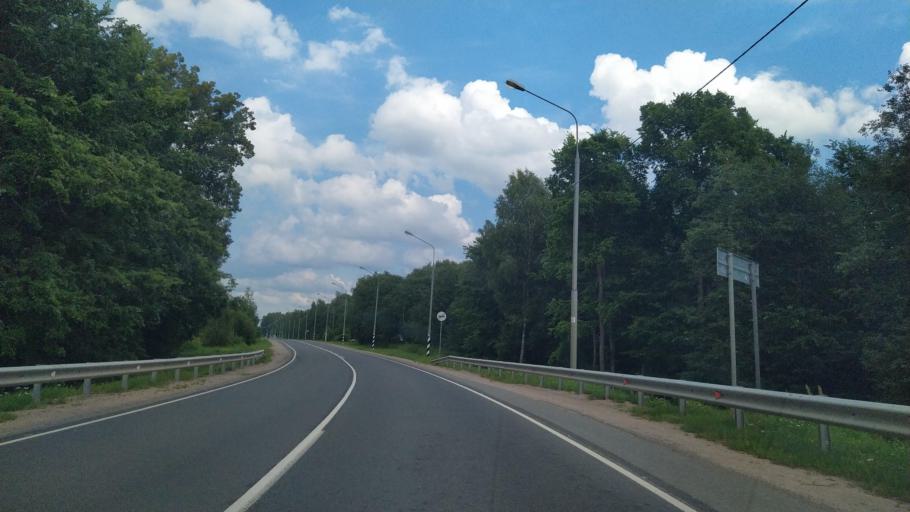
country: RU
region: Pskov
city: Dno
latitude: 58.0514
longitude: 29.9517
